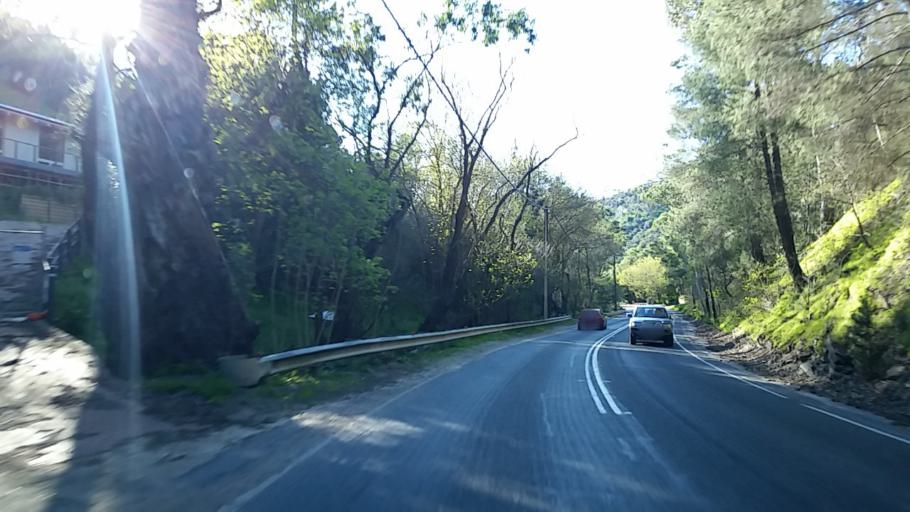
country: AU
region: South Australia
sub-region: Adelaide Hills
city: Adelaide Hills
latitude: -34.9191
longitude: 138.6956
